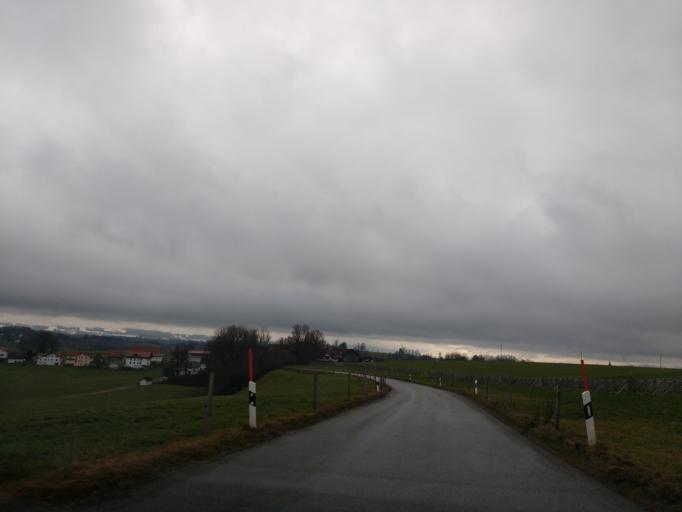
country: DE
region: Bavaria
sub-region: Swabia
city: Neuburg
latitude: 47.7406
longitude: 10.3524
